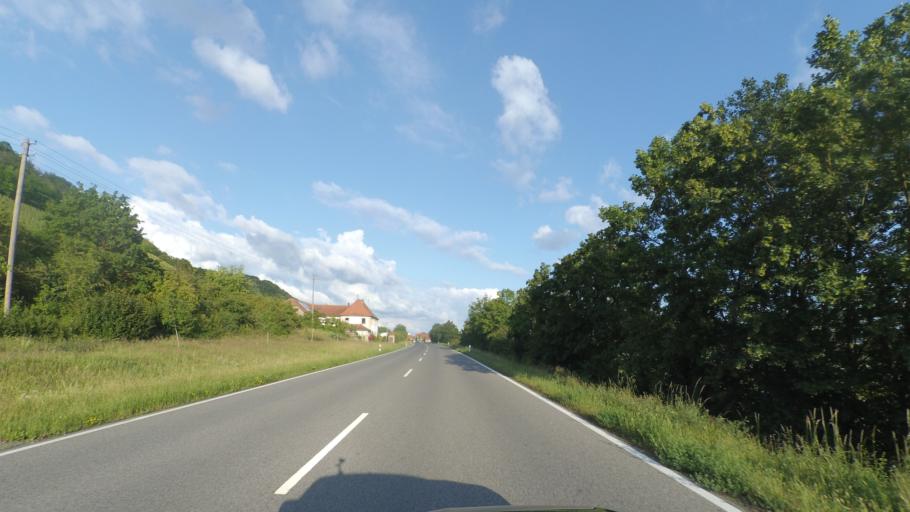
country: DE
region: Bavaria
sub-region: Regierungsbezirk Unterfranken
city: Zeil
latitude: 50.0029
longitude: 10.6085
